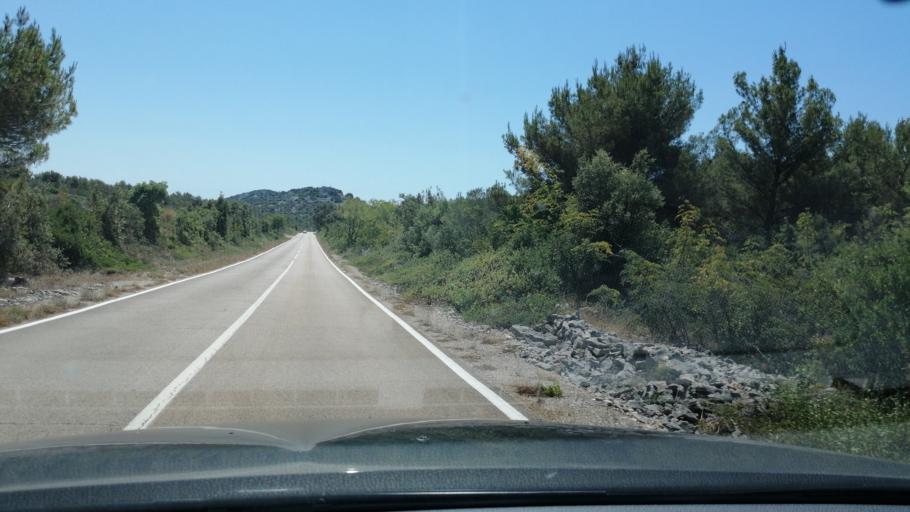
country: HR
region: Sibensko-Kniniska
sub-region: Grad Sibenik
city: Pirovac
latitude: 43.8438
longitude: 15.6872
